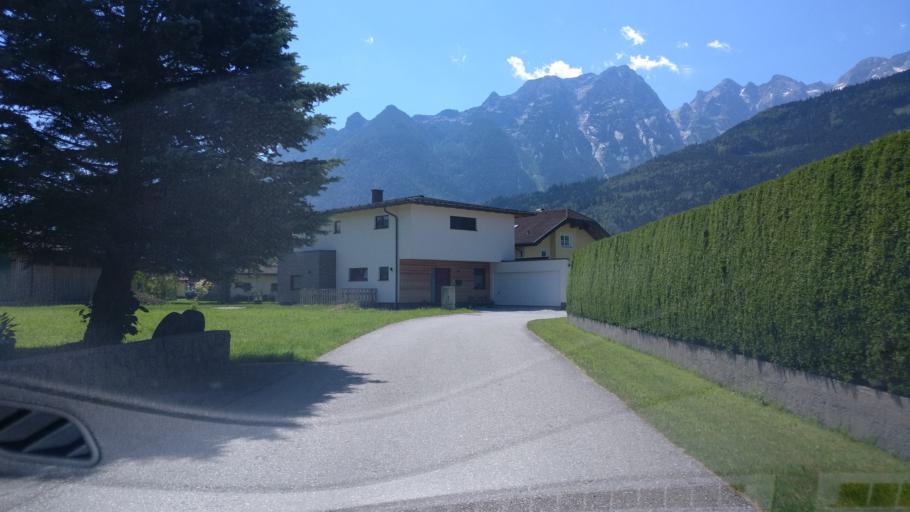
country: AT
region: Salzburg
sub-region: Politischer Bezirk Hallein
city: Kuchl
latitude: 47.6321
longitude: 13.1436
